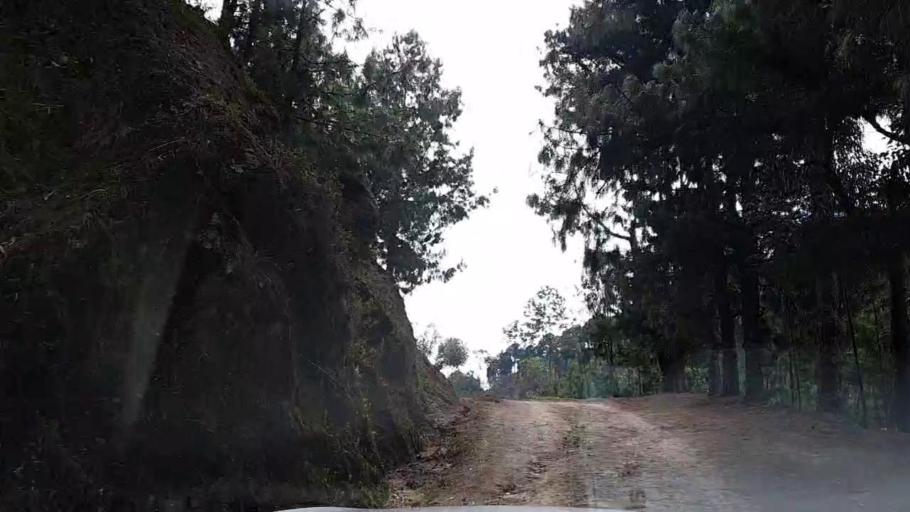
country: RW
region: Southern Province
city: Nzega
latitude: -2.4111
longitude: 29.4571
